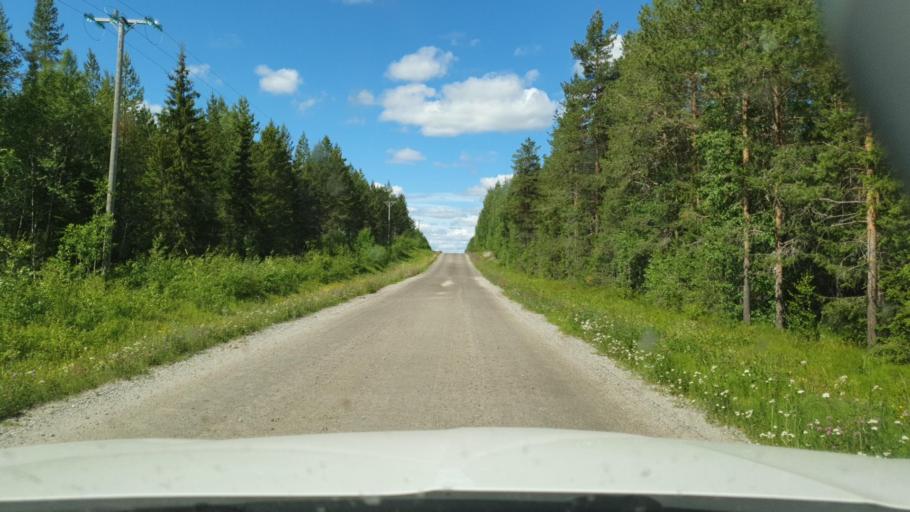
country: SE
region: Vaesterbotten
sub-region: Skelleftea Kommun
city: Backa
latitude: 65.1682
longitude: 21.1211
